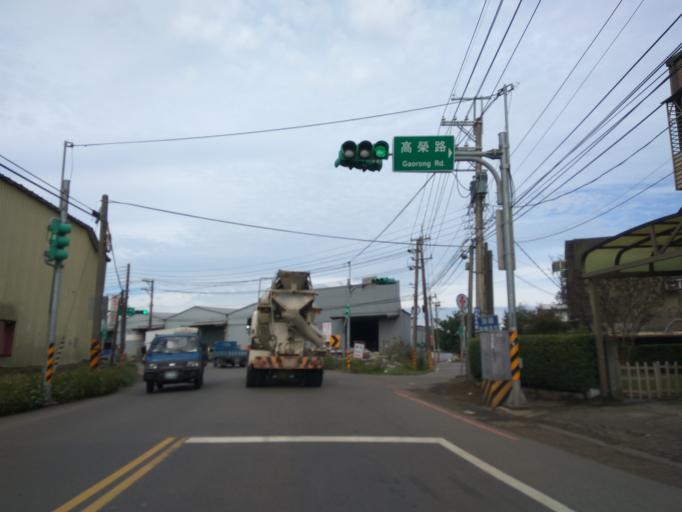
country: TW
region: Taiwan
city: Daxi
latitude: 24.9414
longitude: 121.1579
